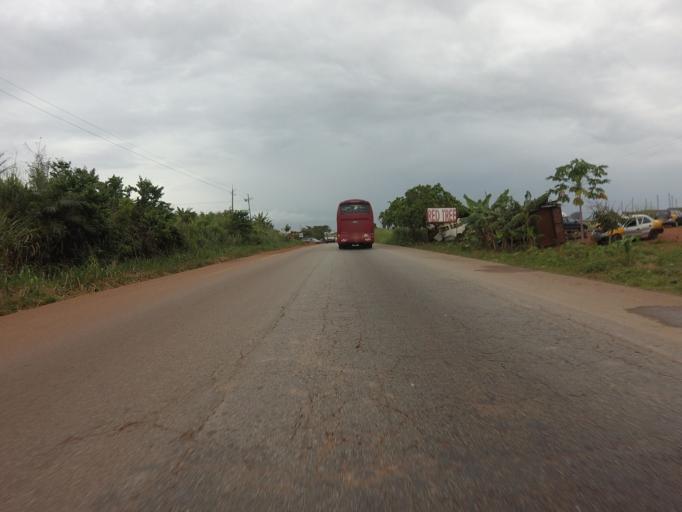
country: GH
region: Ashanti
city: Konongo
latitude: 6.6173
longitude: -1.1822
